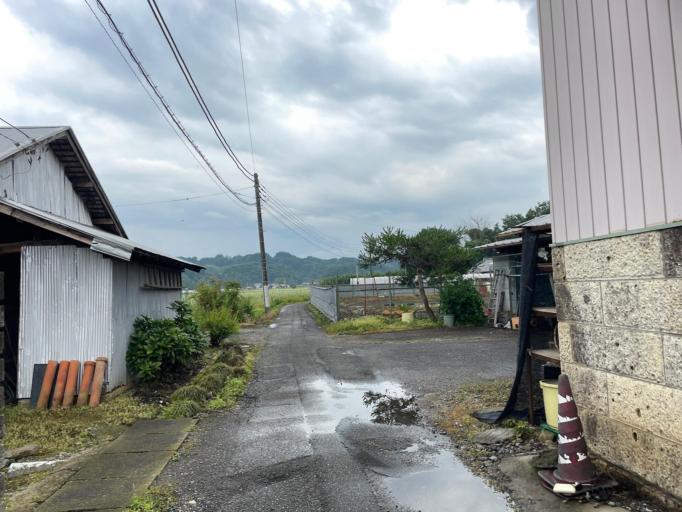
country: JP
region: Tochigi
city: Kanuma
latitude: 36.5221
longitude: 139.7504
